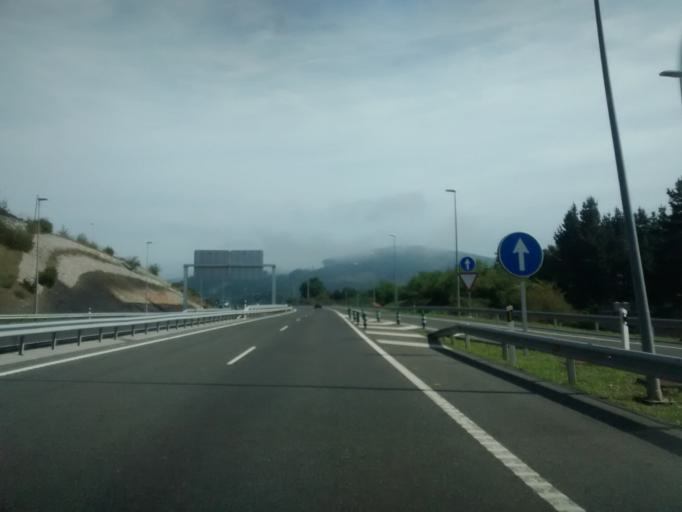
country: ES
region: Basque Country
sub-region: Provincia de Guipuzcoa
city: Aretxabaleta
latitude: 43.0283
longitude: -2.5136
